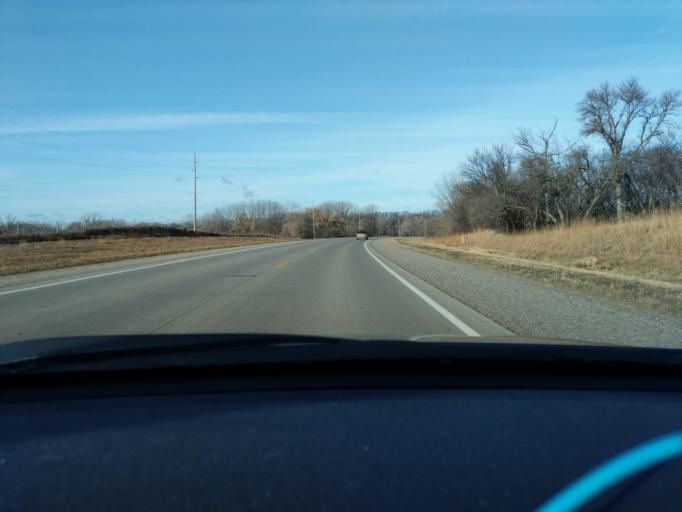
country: US
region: Minnesota
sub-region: Yellow Medicine County
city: Granite Falls
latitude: 44.7894
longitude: -95.4473
